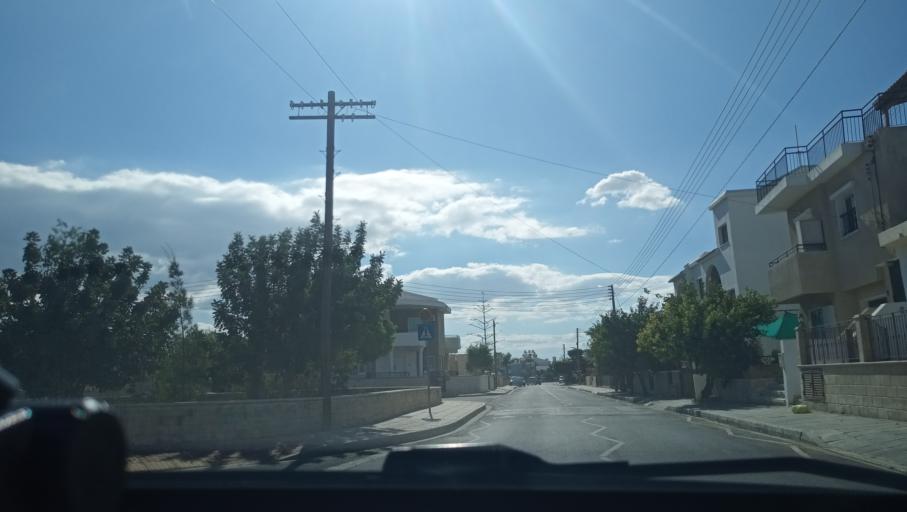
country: CY
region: Larnaka
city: Livadia
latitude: 34.9463
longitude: 33.6259
